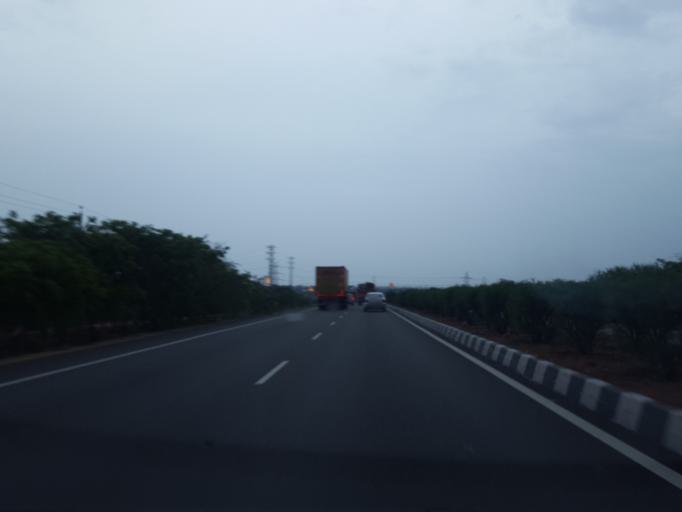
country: IN
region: Telangana
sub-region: Mahbubnagar
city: Farrukhnagar
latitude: 17.0995
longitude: 78.2499
